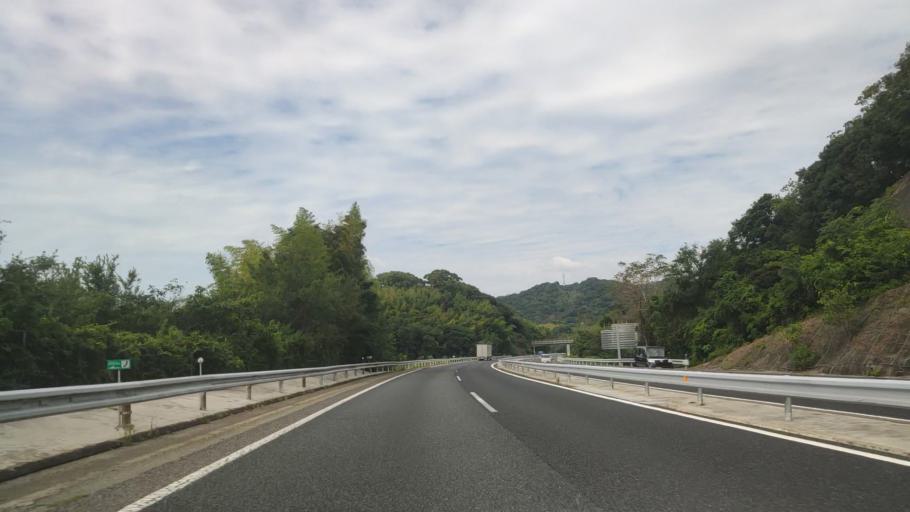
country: JP
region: Wakayama
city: Wakayama-shi
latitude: 34.2135
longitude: 135.2249
